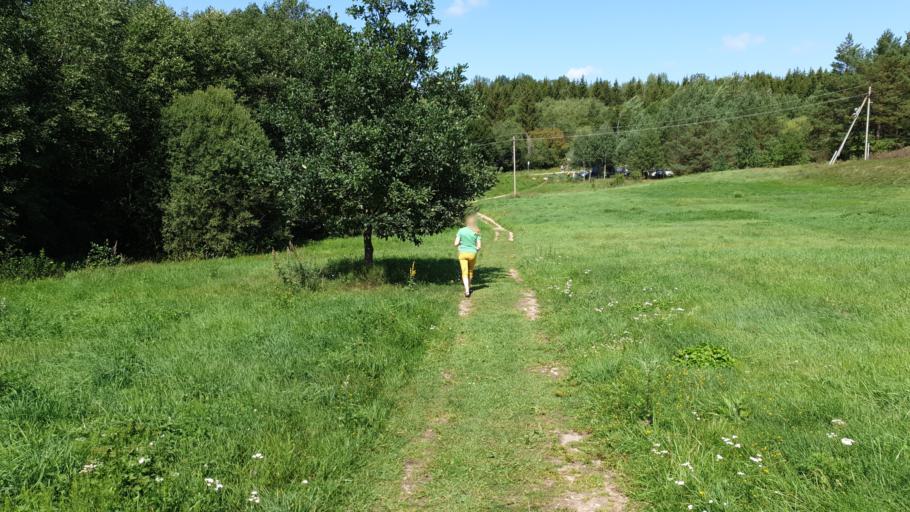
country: LT
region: Vilnius County
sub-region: Vilniaus Rajonas
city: Vievis
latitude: 54.8254
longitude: 24.9457
